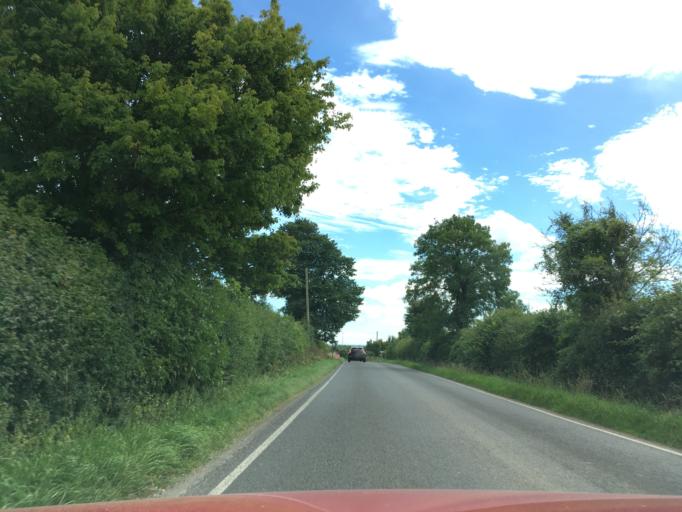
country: GB
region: England
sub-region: Somerset
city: Street
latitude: 51.0839
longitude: -2.6944
